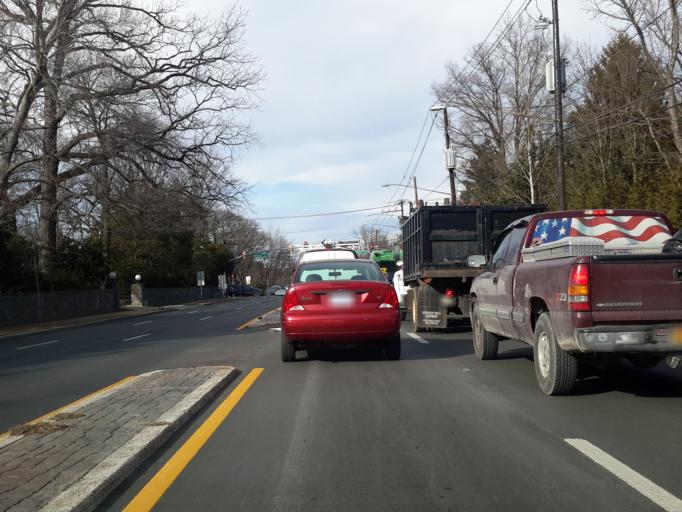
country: US
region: Maryland
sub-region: Montgomery County
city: Chevy Chase
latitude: 38.9756
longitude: -77.0771
